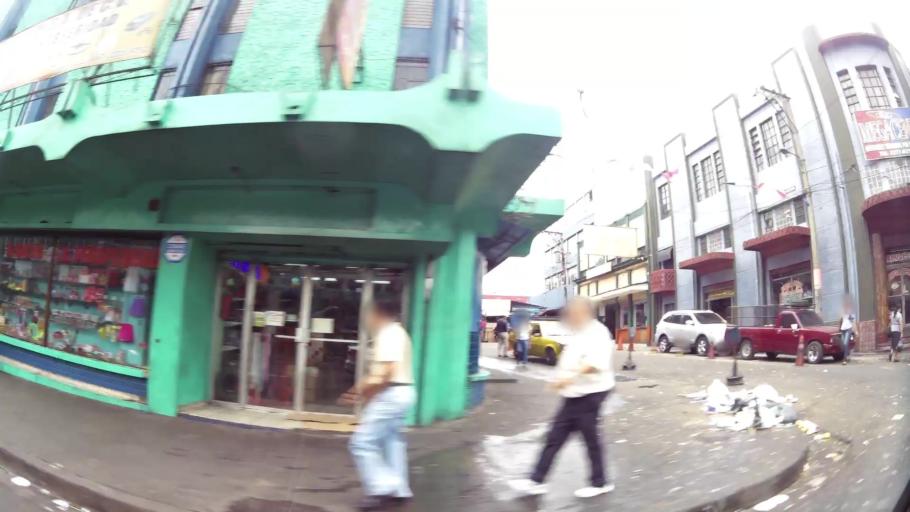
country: SV
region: San Salvador
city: San Salvador
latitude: 13.7001
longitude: -89.1941
